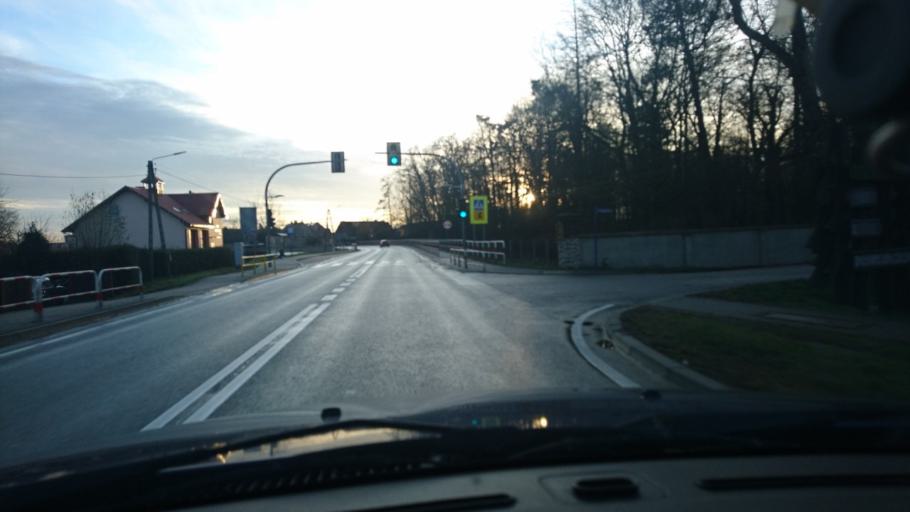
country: PL
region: Greater Poland Voivodeship
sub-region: Powiat kepinski
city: Opatow
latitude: 51.1813
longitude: 18.1446
